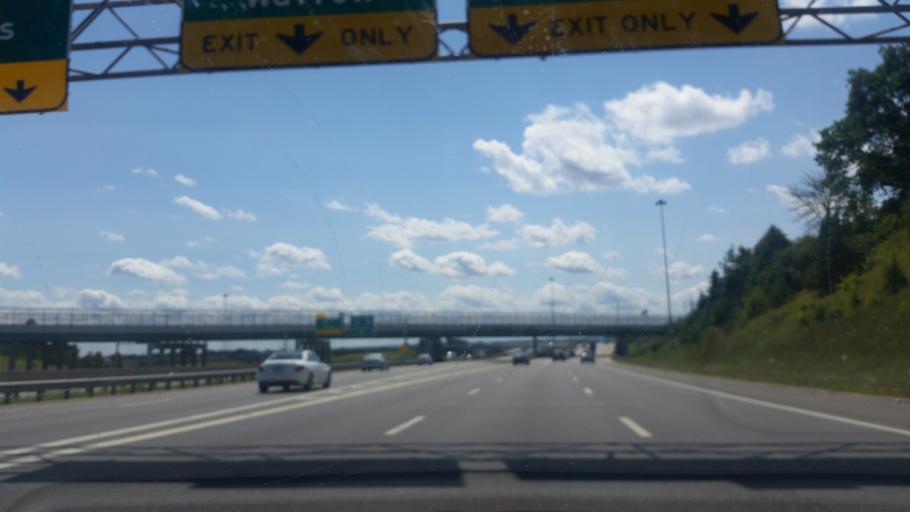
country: US
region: Ohio
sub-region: Cuyahoga County
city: Highland Hills
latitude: 41.4365
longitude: -81.4994
